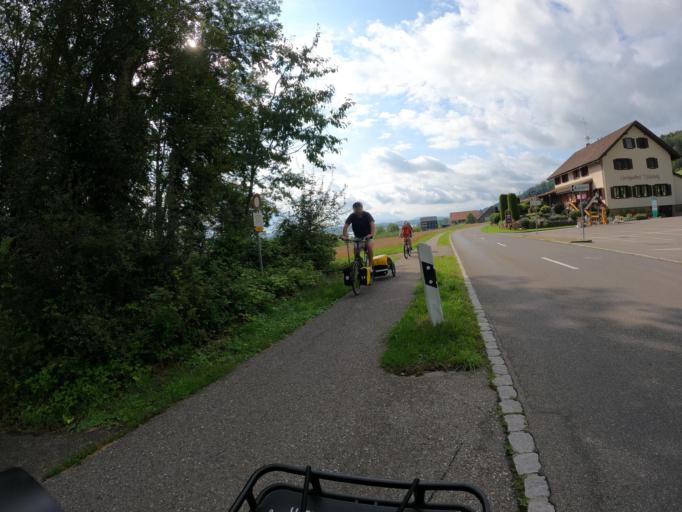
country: CH
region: Lucerne
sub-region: Hochdorf District
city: Roemerswil
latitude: 47.1960
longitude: 8.2517
